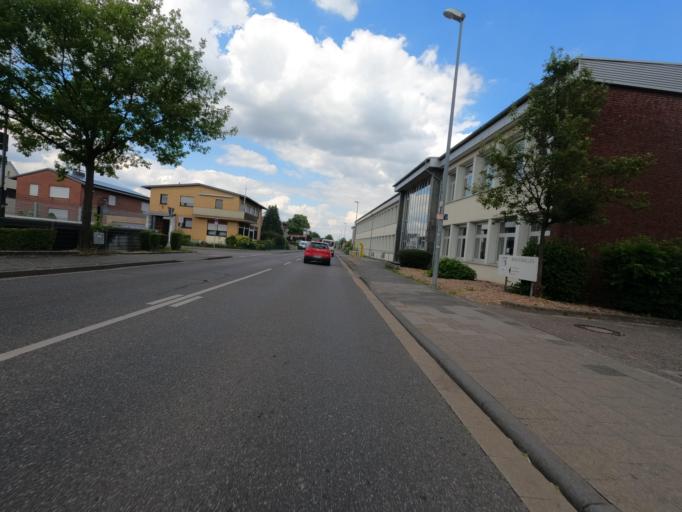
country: DE
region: North Rhine-Westphalia
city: Geilenkirchen
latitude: 50.9681
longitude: 6.1120
